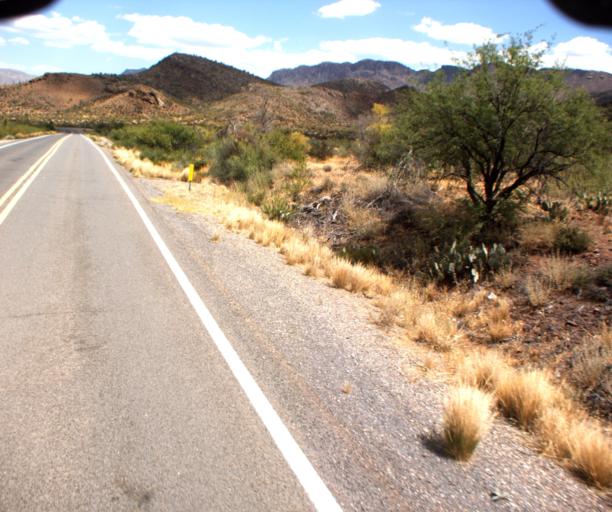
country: US
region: Arizona
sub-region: Pinal County
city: Superior
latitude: 33.2439
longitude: -111.0960
